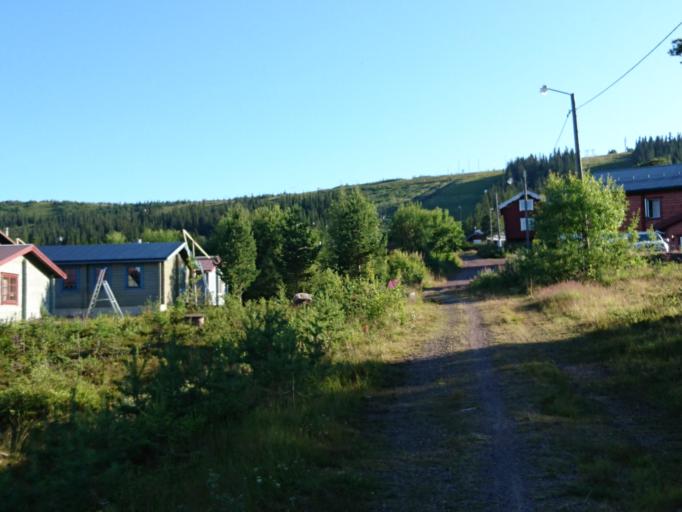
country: SE
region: Dalarna
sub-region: Malung-Saelens kommun
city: Malung
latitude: 61.1673
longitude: 13.1758
